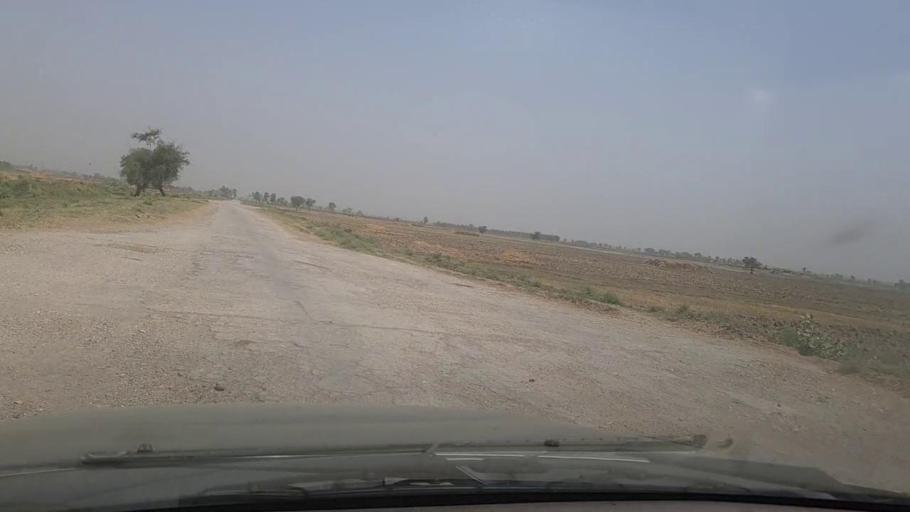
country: PK
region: Sindh
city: Madeji
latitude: 27.8109
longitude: 68.3978
